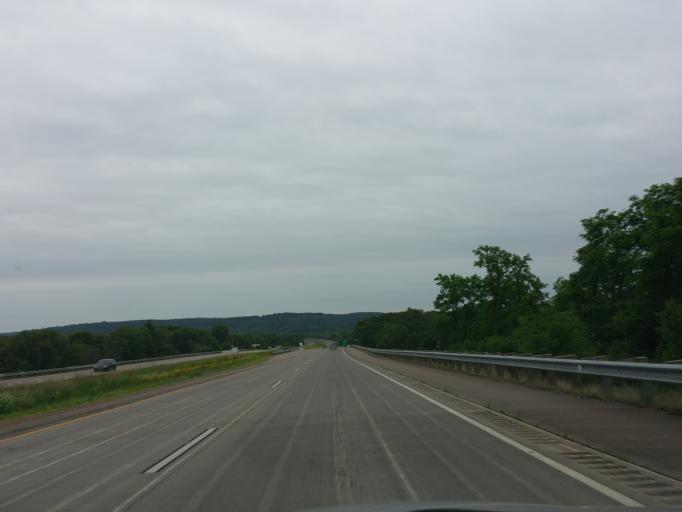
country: US
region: Wisconsin
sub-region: Eau Claire County
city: Eau Claire
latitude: 44.7951
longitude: -91.5511
